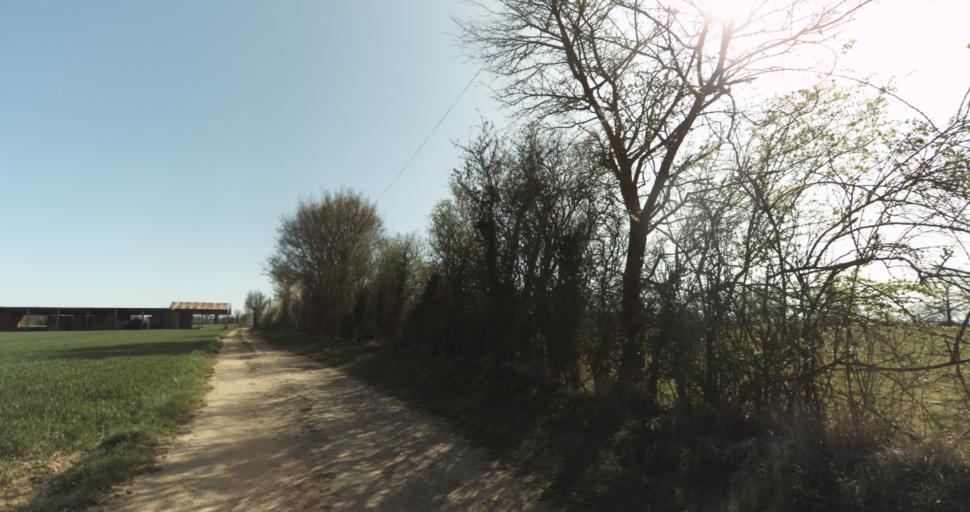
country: FR
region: Lower Normandy
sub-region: Departement du Calvados
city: Saint-Pierre-sur-Dives
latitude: 48.9312
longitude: -0.0082
